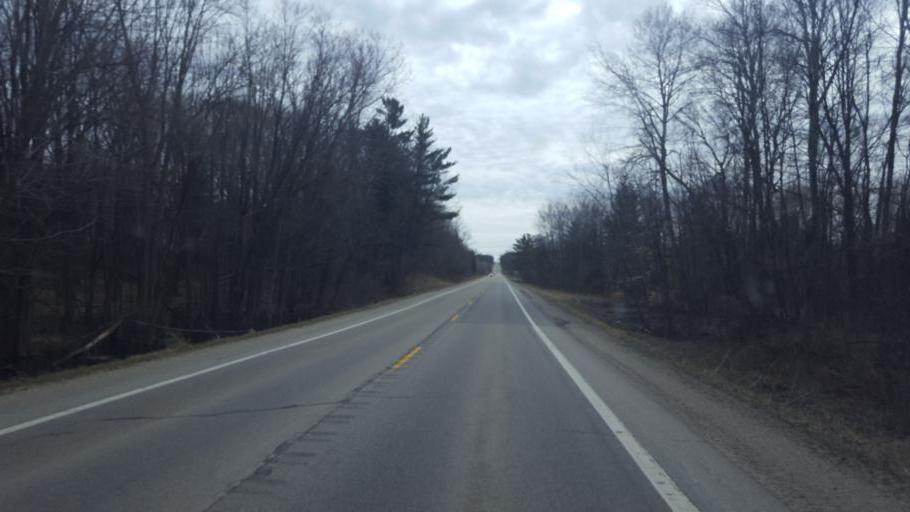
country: US
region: Michigan
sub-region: Isabella County
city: Lake Isabella
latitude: 43.6951
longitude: -85.1467
